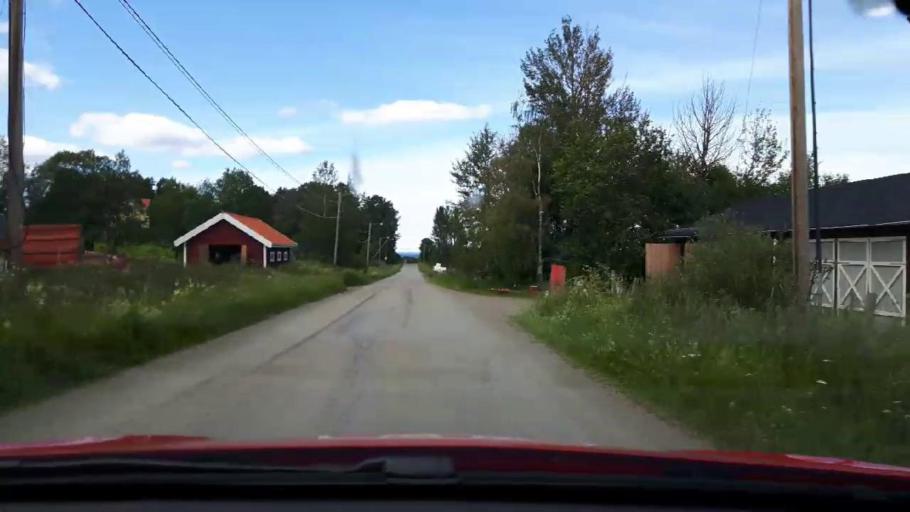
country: SE
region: Jaemtland
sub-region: Bergs Kommun
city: Hoverberg
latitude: 62.8214
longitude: 14.4605
